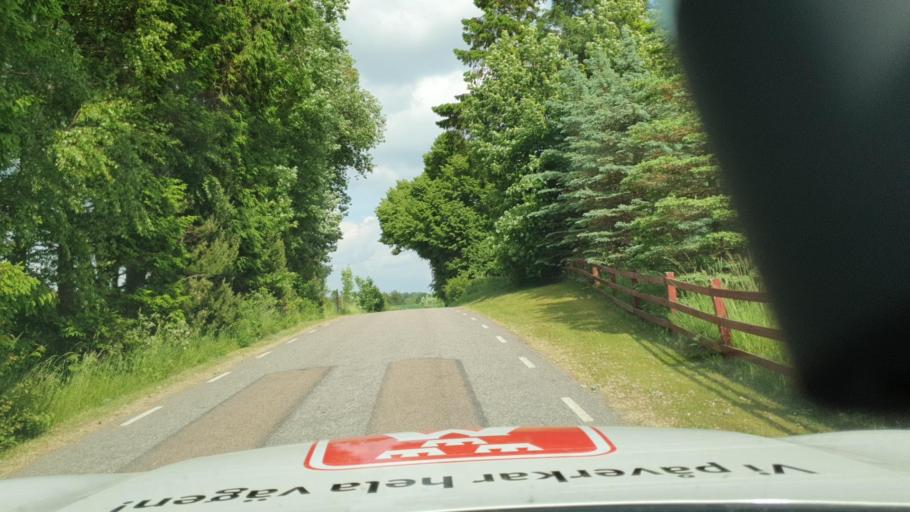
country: SE
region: Skane
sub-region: Skurups Kommun
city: Skurup
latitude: 55.5211
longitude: 13.4645
